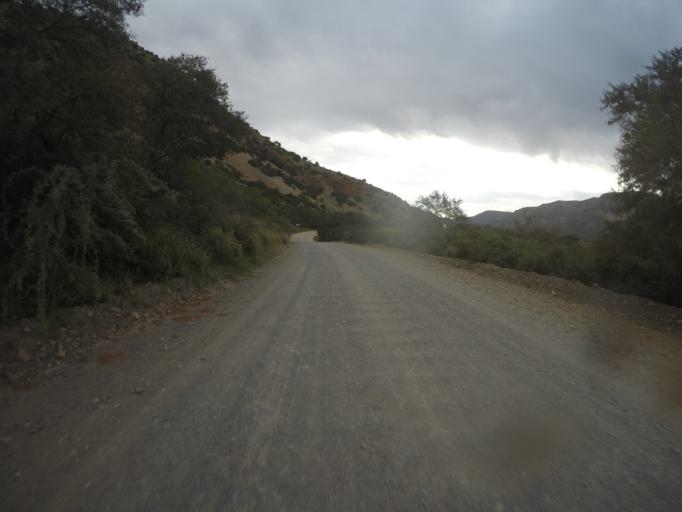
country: ZA
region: Eastern Cape
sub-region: Cacadu District Municipality
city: Willowmore
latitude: -33.5249
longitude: 23.8463
